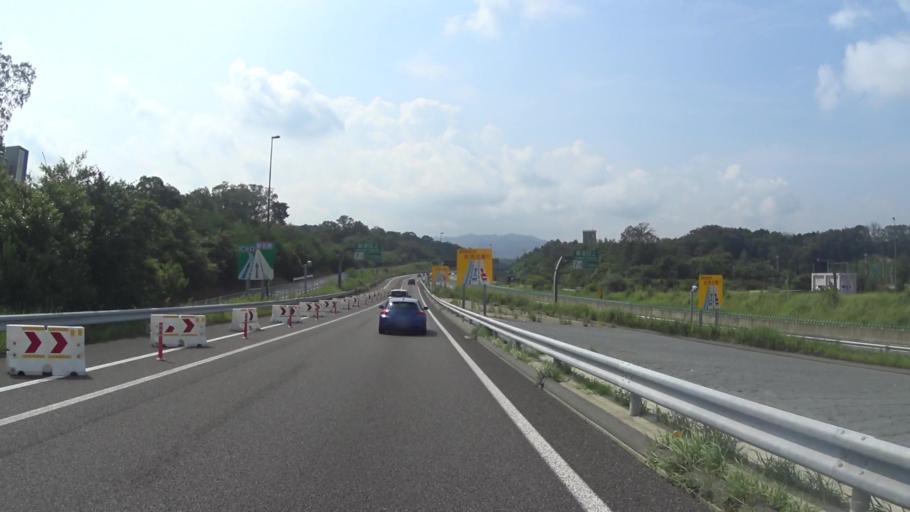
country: JP
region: Shiga Prefecture
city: Kusatsu
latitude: 34.9806
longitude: 135.9603
